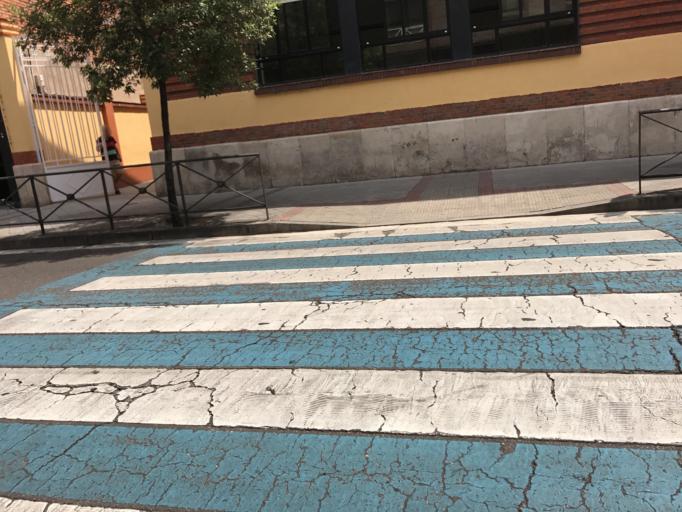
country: ES
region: Castille and Leon
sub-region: Provincia de Valladolid
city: Valladolid
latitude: 41.6458
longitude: -4.7174
